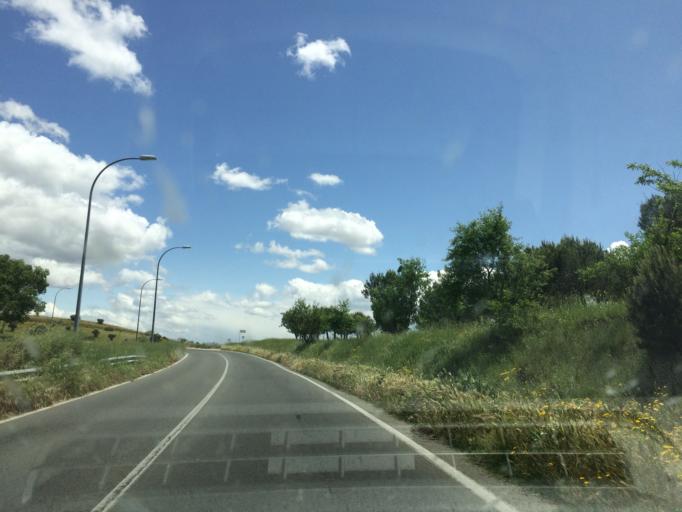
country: ES
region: Madrid
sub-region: Provincia de Madrid
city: Valdeolmos
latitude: 40.6930
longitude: -3.4424
